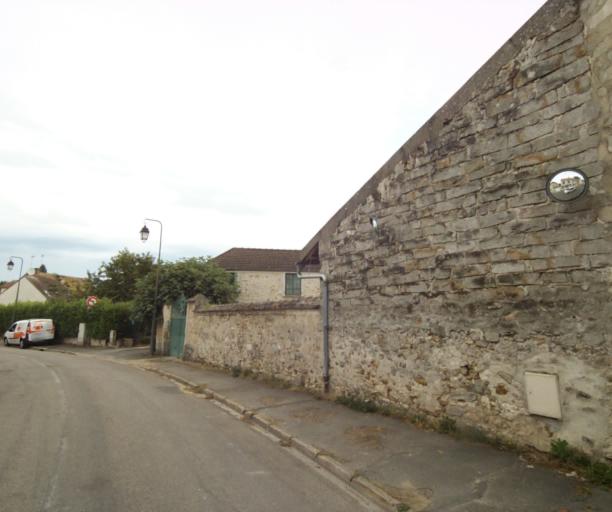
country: FR
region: Ile-de-France
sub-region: Departement de Seine-et-Marne
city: Cely
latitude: 48.4582
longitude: 2.5376
